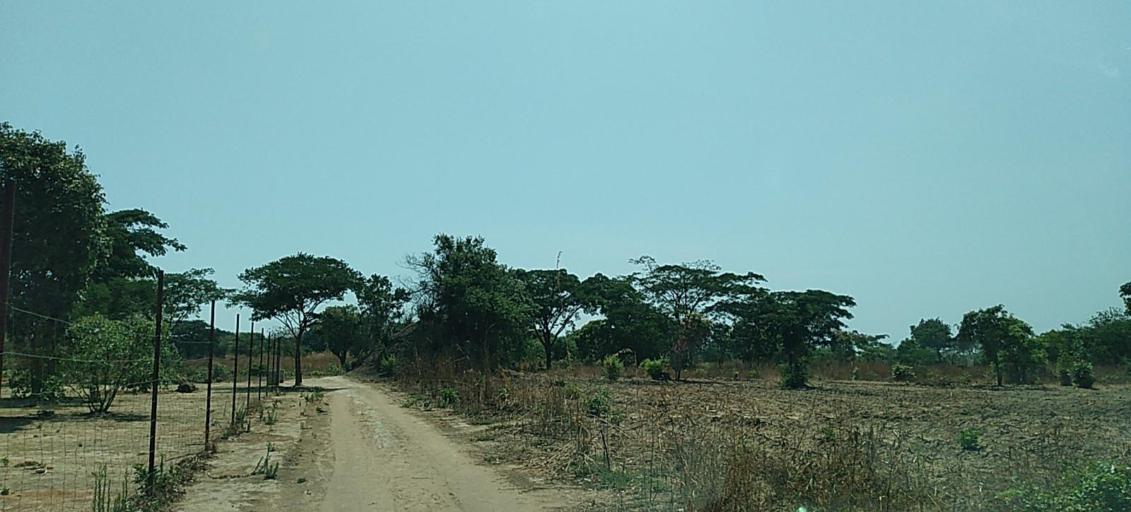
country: ZM
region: Copperbelt
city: Luanshya
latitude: -13.0074
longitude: 28.4746
